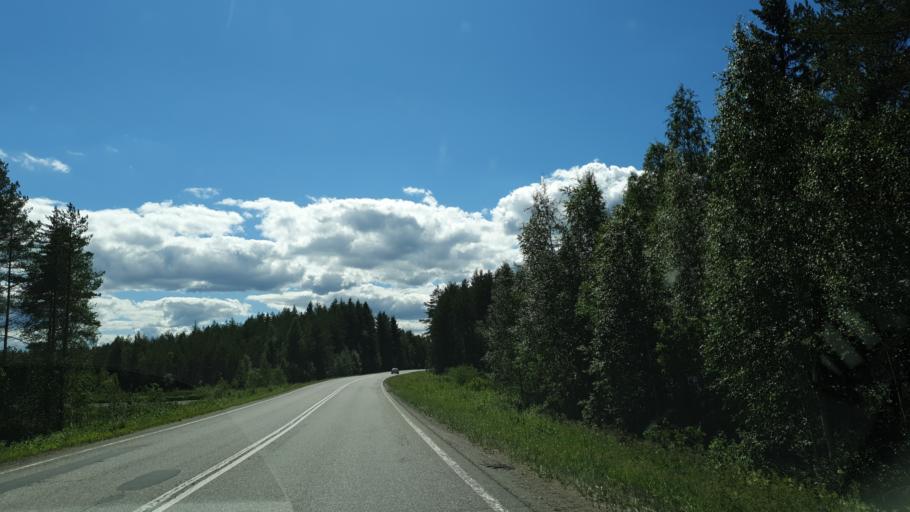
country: FI
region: Northern Savo
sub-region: Koillis-Savo
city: Juankoski
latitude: 63.2699
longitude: 28.3115
